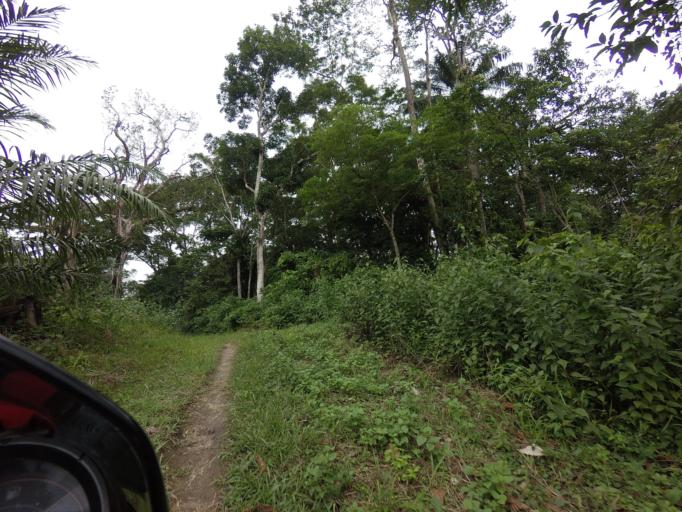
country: SL
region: Eastern Province
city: Mobai
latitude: 7.9870
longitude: -10.7031
